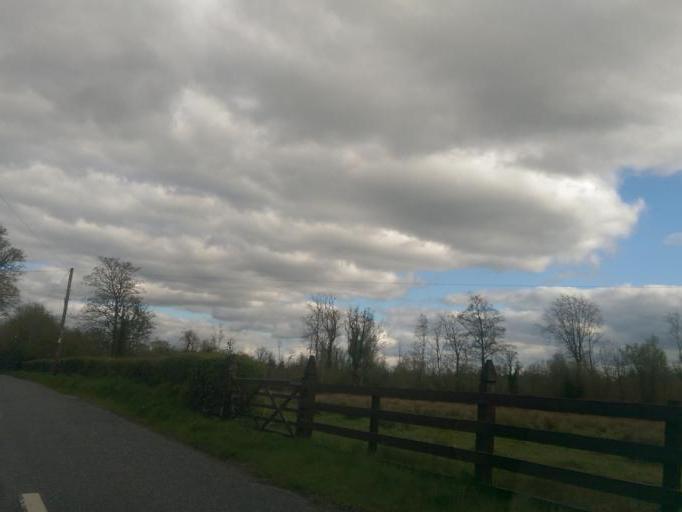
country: IE
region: Connaught
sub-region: County Galway
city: Ballinasloe
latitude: 53.4184
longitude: -8.3833
